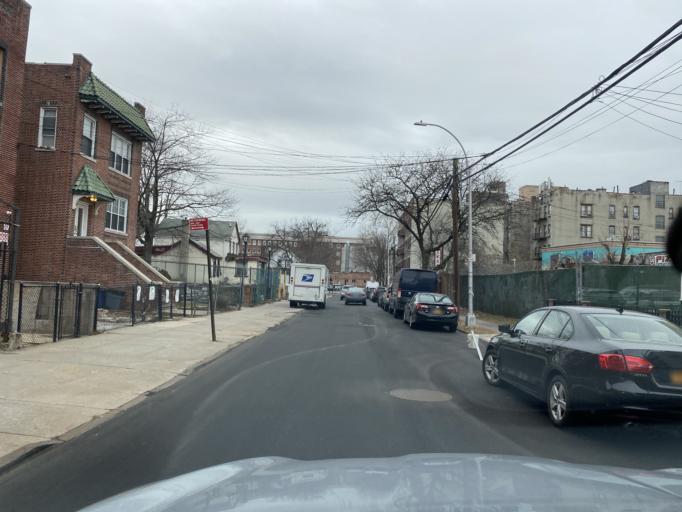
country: US
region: New York
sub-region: Bronx
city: The Bronx
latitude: 40.8593
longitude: -73.8852
